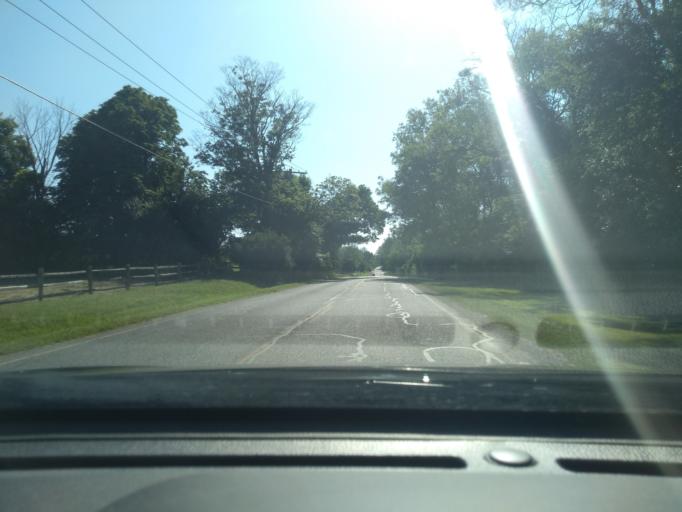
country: US
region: New York
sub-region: Erie County
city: Billington Heights
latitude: 42.7786
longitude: -78.6698
